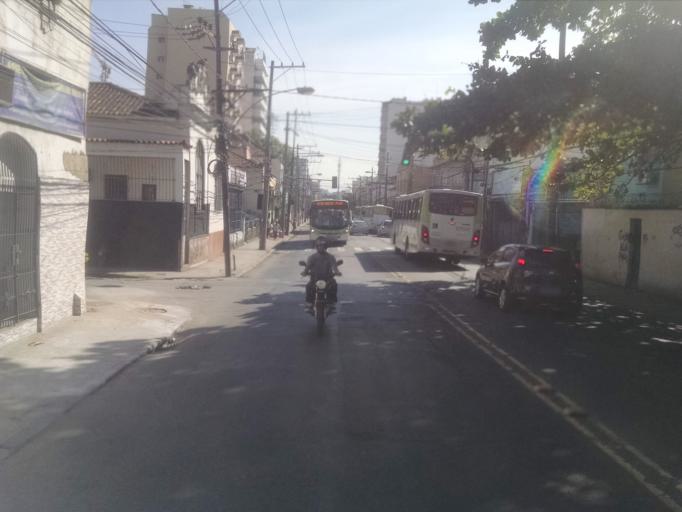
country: BR
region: Rio de Janeiro
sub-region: Rio De Janeiro
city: Rio de Janeiro
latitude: -22.9137
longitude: -43.2641
